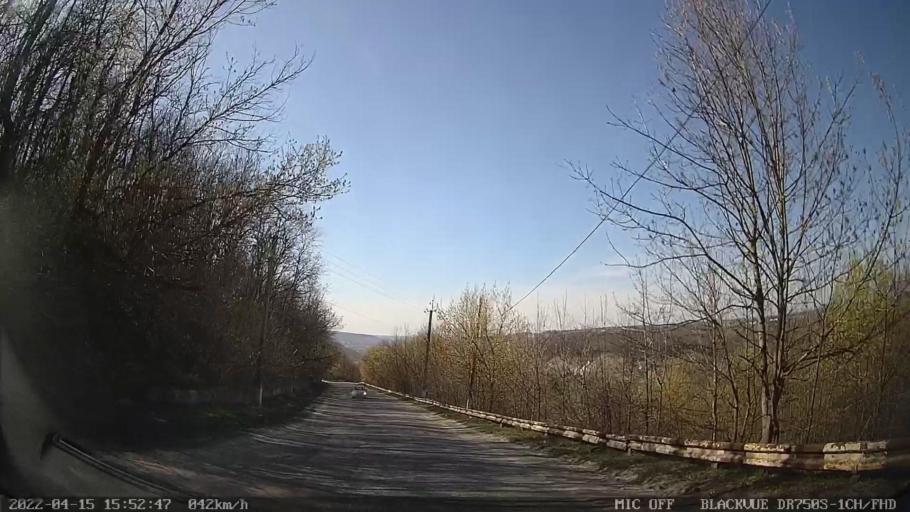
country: MD
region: Raionul Ocnita
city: Otaci
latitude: 48.3962
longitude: 27.8906
